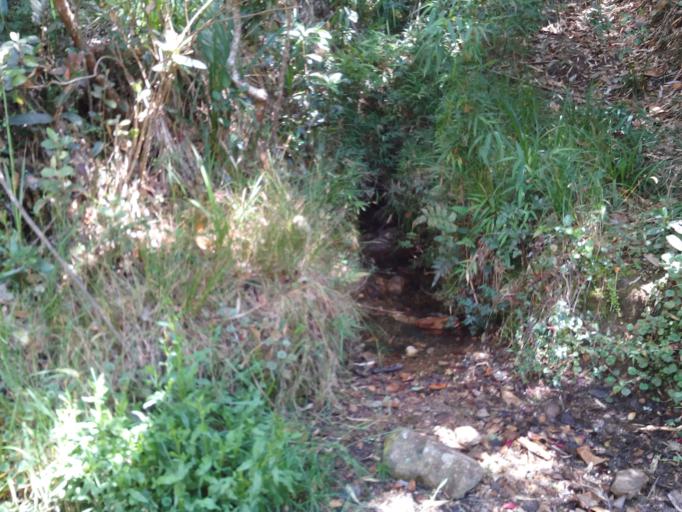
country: CO
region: Bogota D.C.
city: Bogota
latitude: 4.6031
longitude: -74.0359
